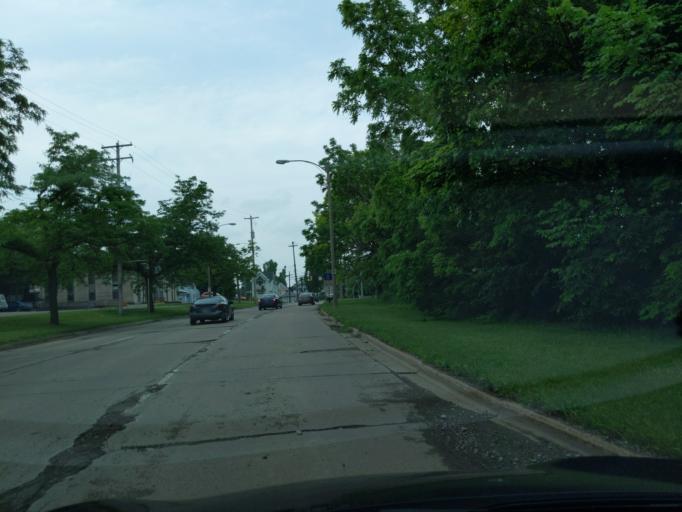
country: US
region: Michigan
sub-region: Ingham County
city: Lansing
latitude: 42.7423
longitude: -84.5508
